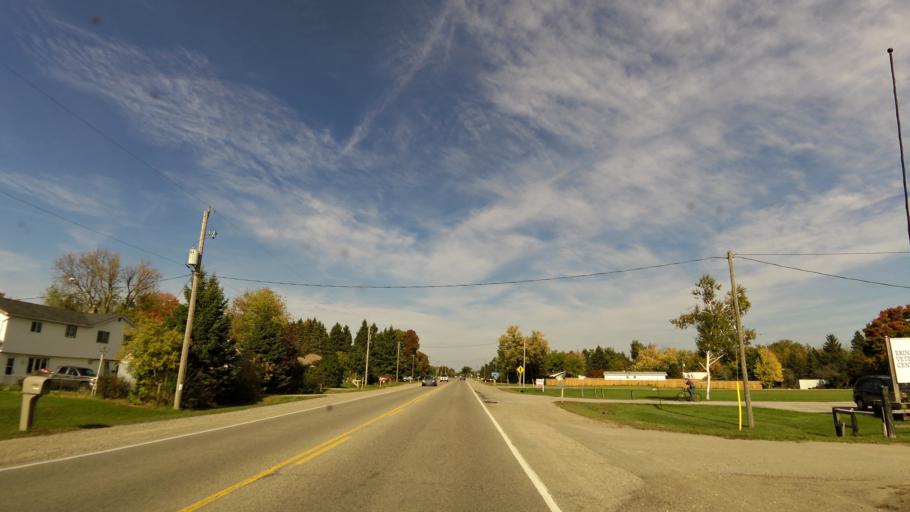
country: CA
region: Ontario
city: Orangeville
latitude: 43.7520
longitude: -80.0678
